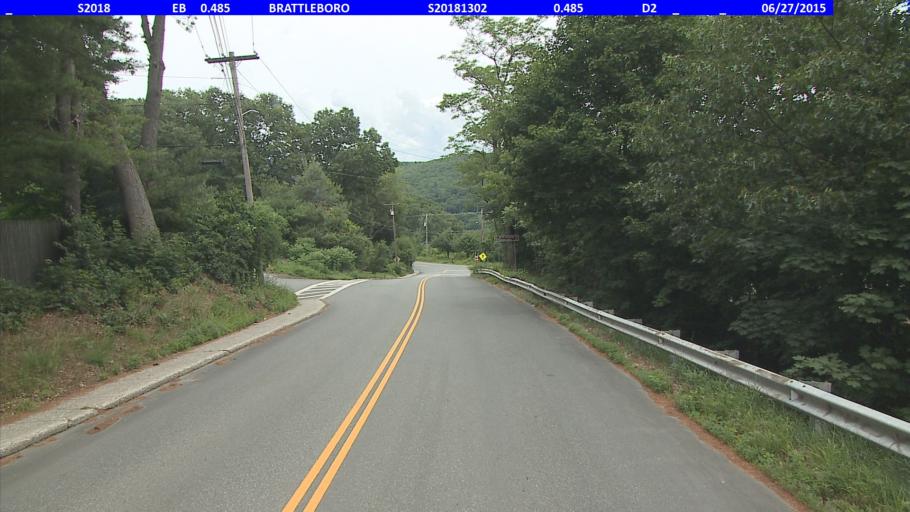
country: US
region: Vermont
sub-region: Windham County
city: Brattleboro
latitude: 42.8371
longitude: -72.5567
